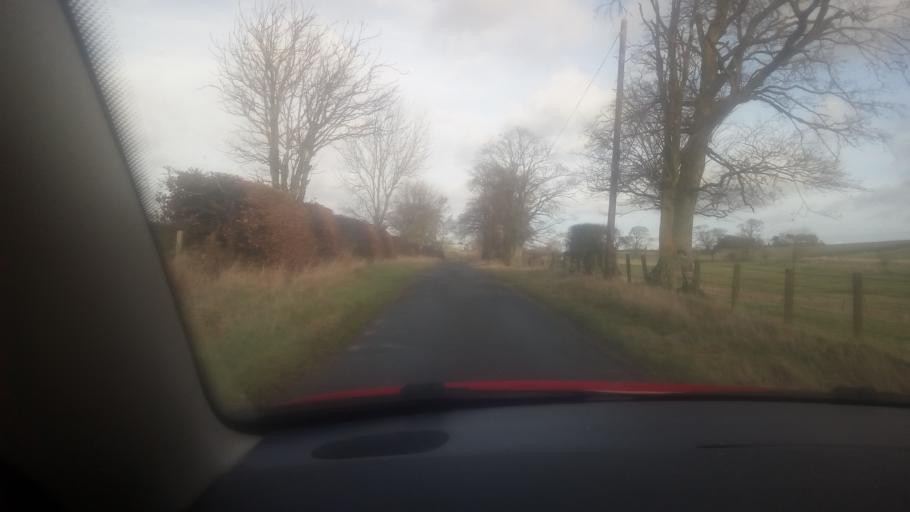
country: GB
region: Scotland
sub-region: The Scottish Borders
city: Kelso
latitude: 55.4994
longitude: -2.4258
